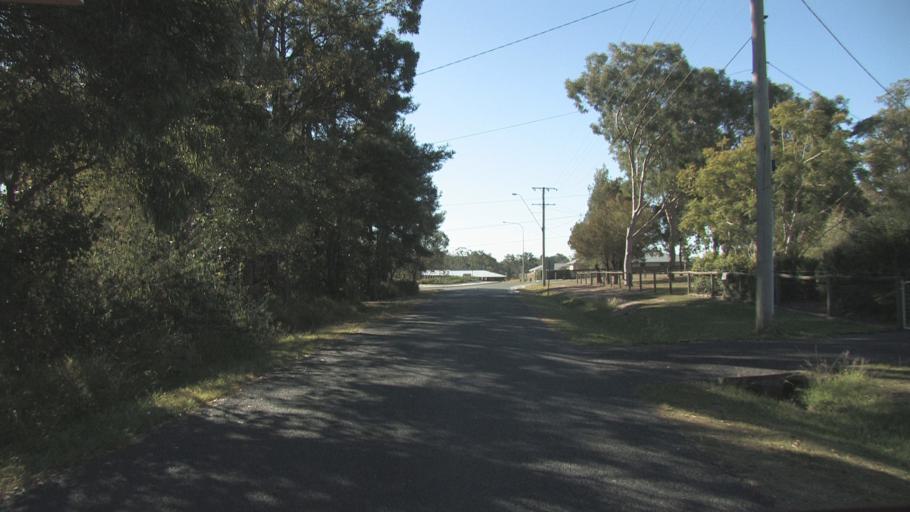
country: AU
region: Queensland
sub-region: Logan
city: Logan Reserve
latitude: -27.7138
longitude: 153.1075
